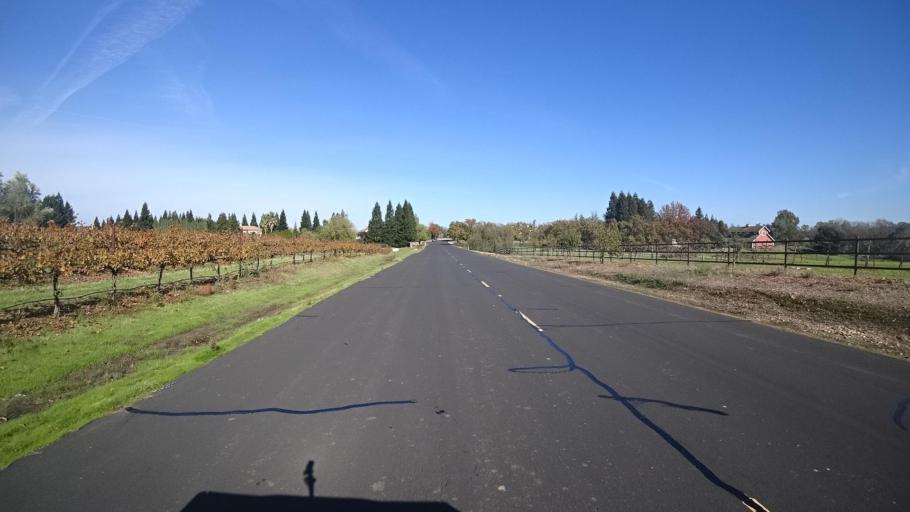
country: US
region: California
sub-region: Sacramento County
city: Wilton
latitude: 38.4291
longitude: -121.2765
